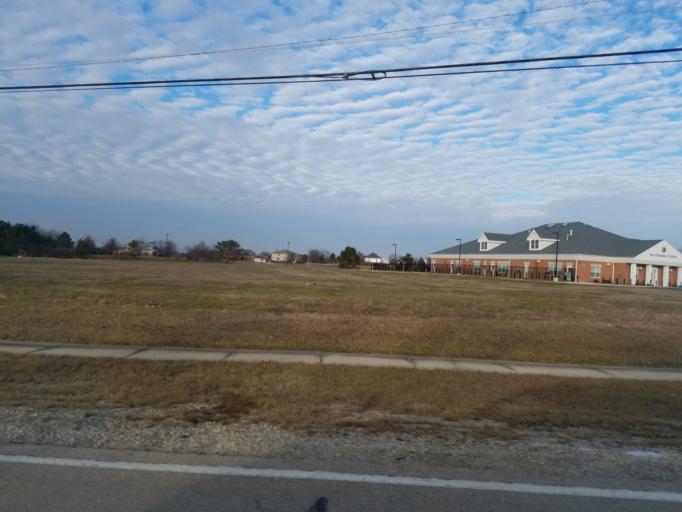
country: US
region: Illinois
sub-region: Will County
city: Mokena
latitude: 41.5288
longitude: -87.9079
